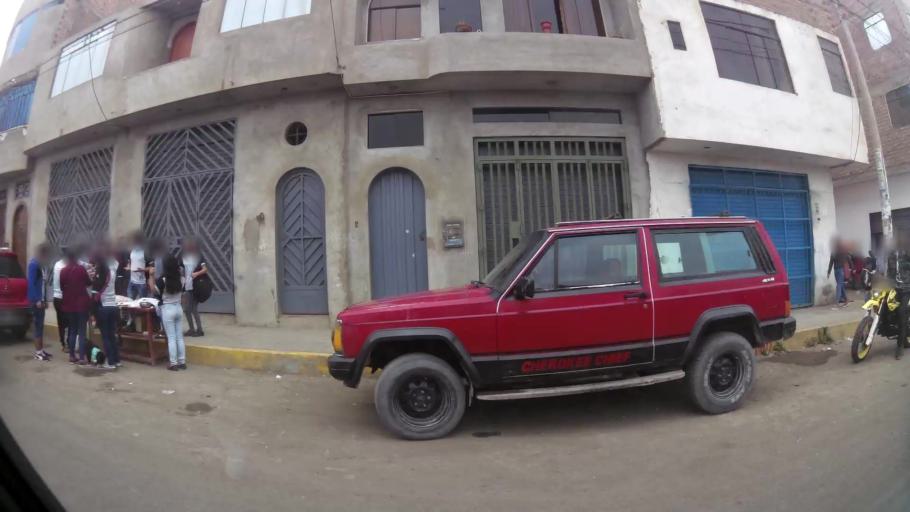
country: PE
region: Lima
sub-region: Provincia de Huaral
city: Huaral
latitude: -11.5025
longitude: -77.2042
